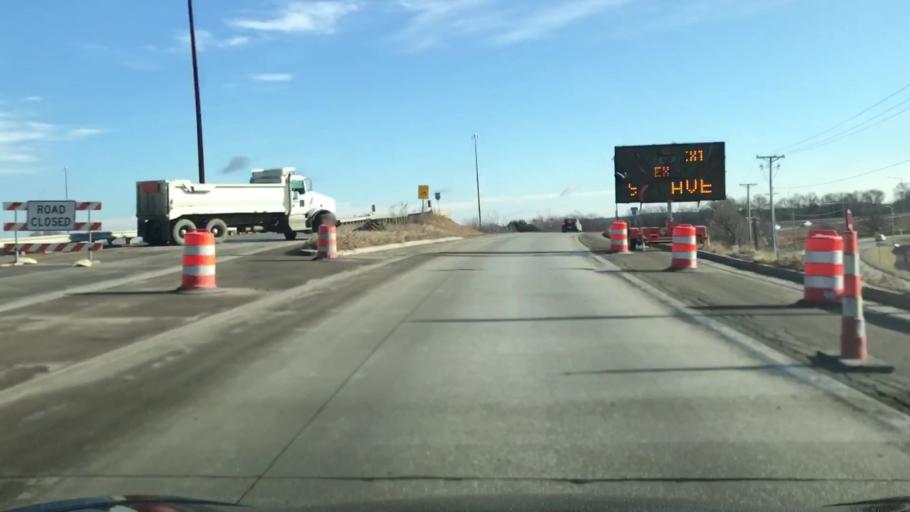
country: US
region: Nebraska
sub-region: Douglas County
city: Omaha
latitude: 41.2614
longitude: -95.9121
